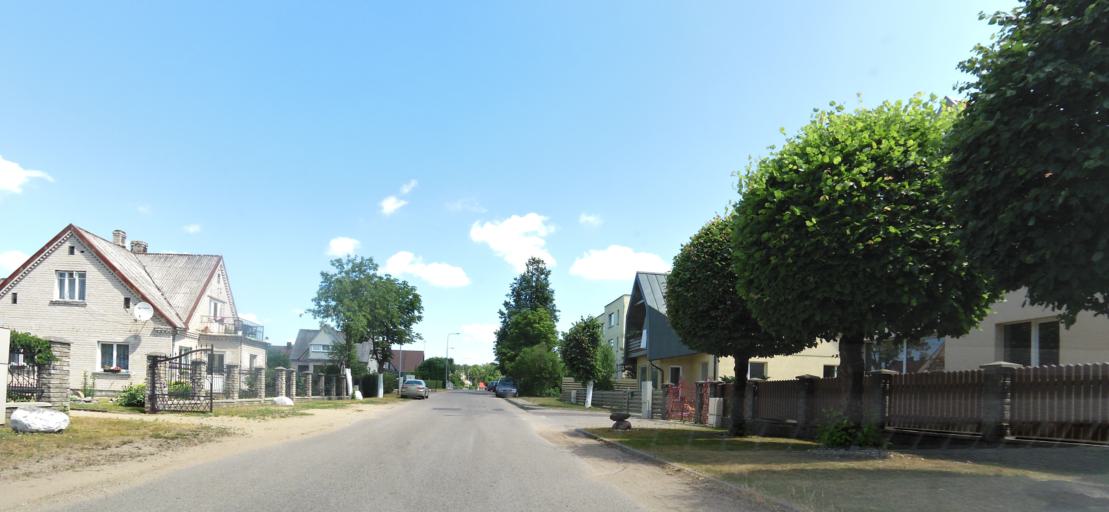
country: LT
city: Nemencine
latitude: 54.8492
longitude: 25.4655
